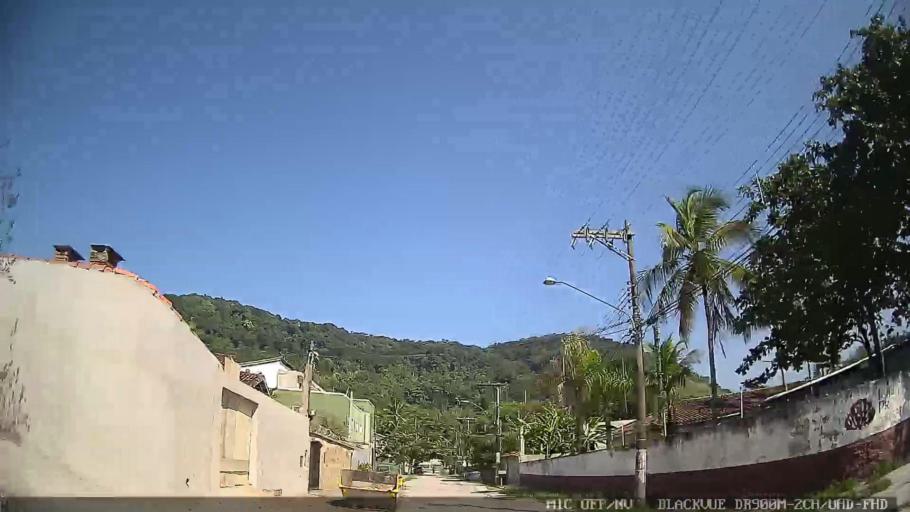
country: BR
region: Sao Paulo
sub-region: Guaruja
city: Guaruja
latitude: -24.0141
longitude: -46.2776
